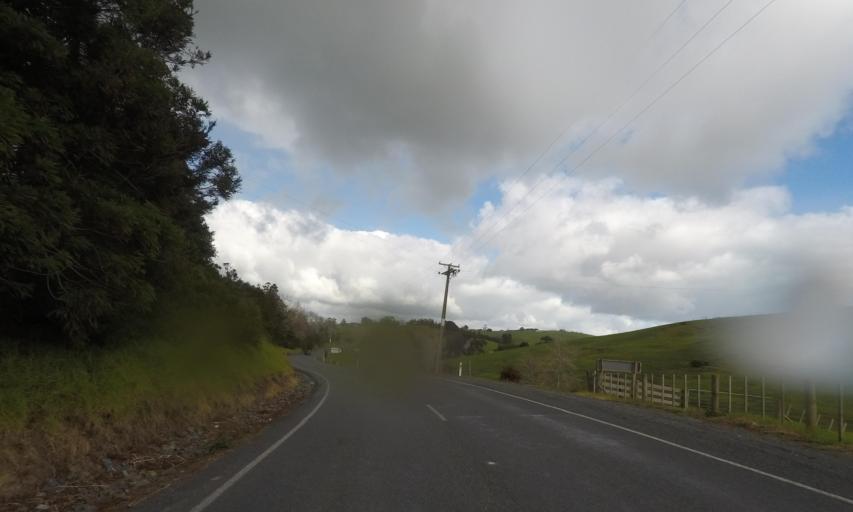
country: NZ
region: Auckland
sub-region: Auckland
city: Wellsford
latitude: -36.1709
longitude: 174.5825
